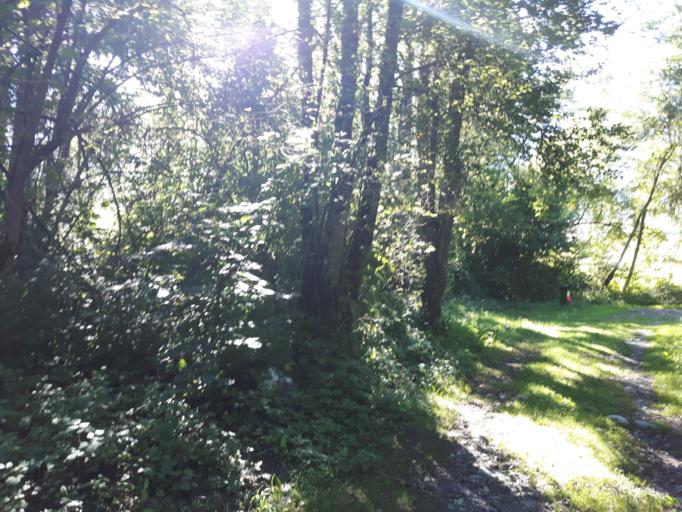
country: CH
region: Grisons
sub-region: Surselva District
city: Ilanz
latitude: 46.7768
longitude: 9.2145
